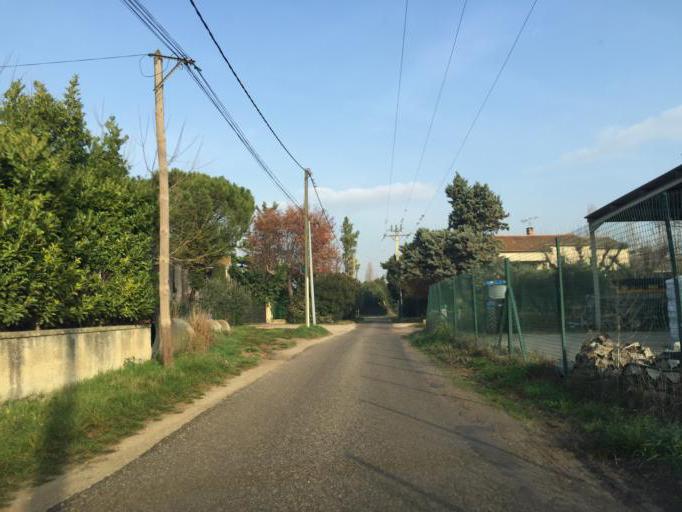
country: FR
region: Provence-Alpes-Cote d'Azur
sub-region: Departement du Vaucluse
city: Bedarrides
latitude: 44.0507
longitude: 4.9075
